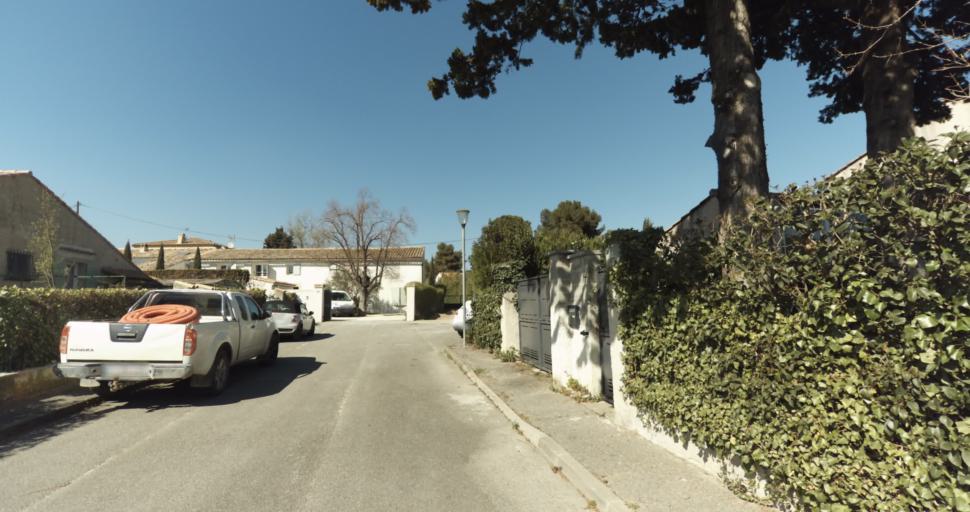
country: FR
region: Provence-Alpes-Cote d'Azur
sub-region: Departement des Bouches-du-Rhone
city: Pelissanne
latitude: 43.6339
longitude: 5.1557
